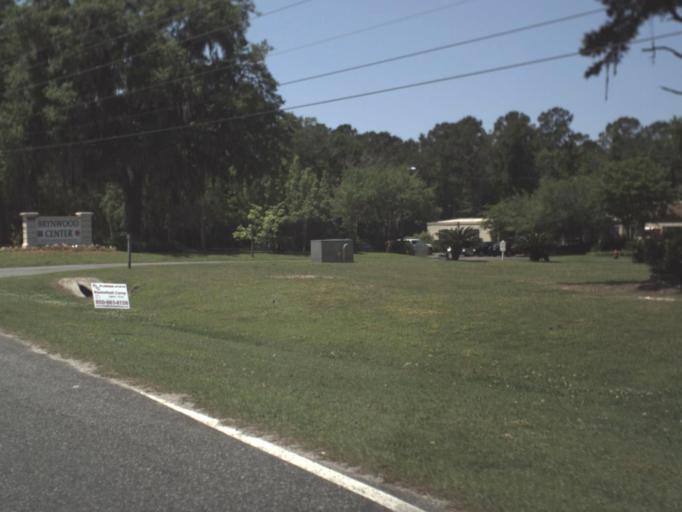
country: US
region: Florida
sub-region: Jefferson County
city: Monticello
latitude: 30.5242
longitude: -83.8729
